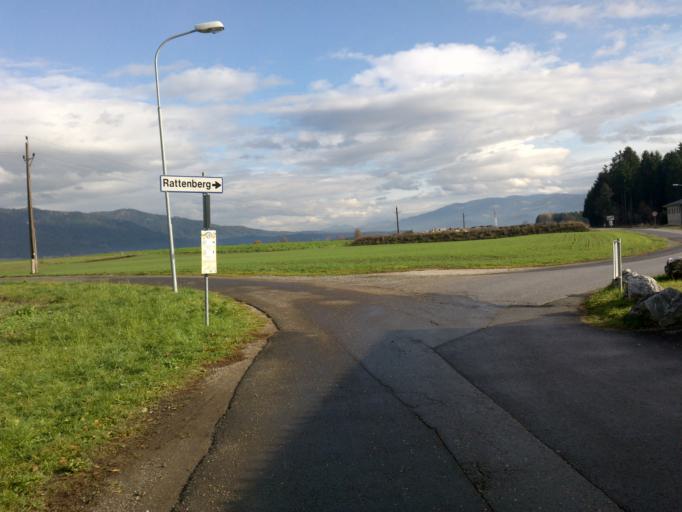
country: AT
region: Styria
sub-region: Politischer Bezirk Murtal
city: Fohnsdorf
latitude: 47.1962
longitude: 14.7143
